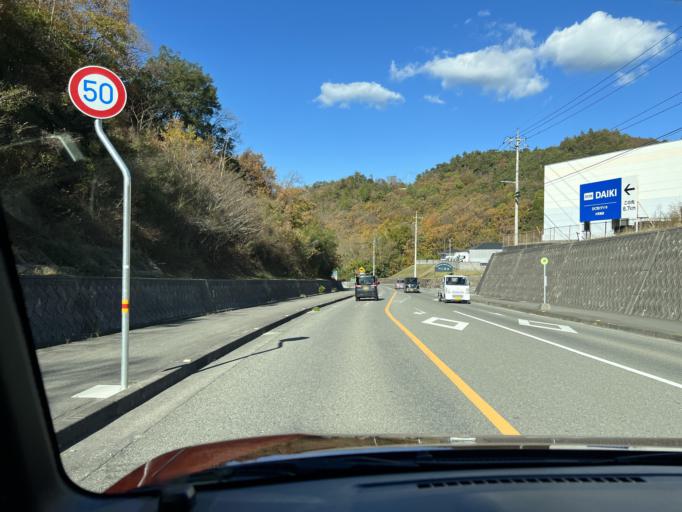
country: JP
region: Kagawa
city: Tonosho
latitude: 34.4771
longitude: 134.2496
